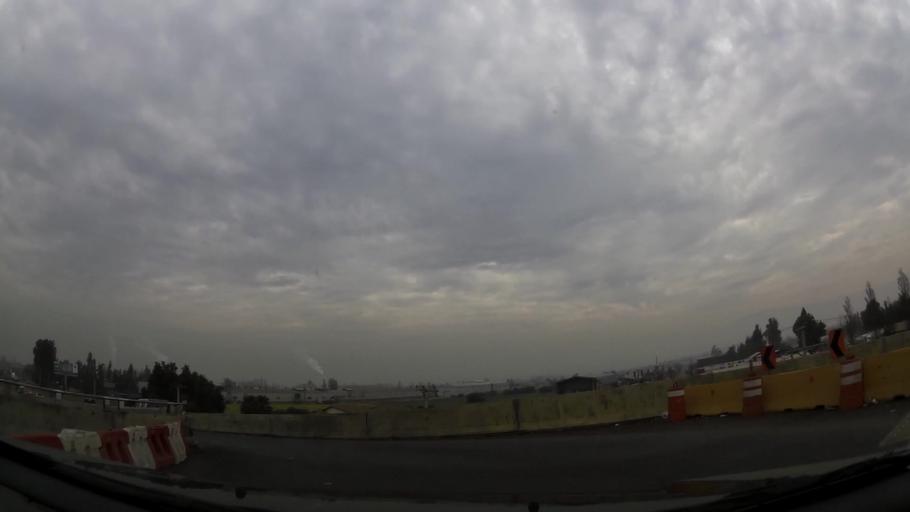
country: CL
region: Santiago Metropolitan
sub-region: Provincia de Chacabuco
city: Chicureo Abajo
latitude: -33.2590
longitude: -70.7486
